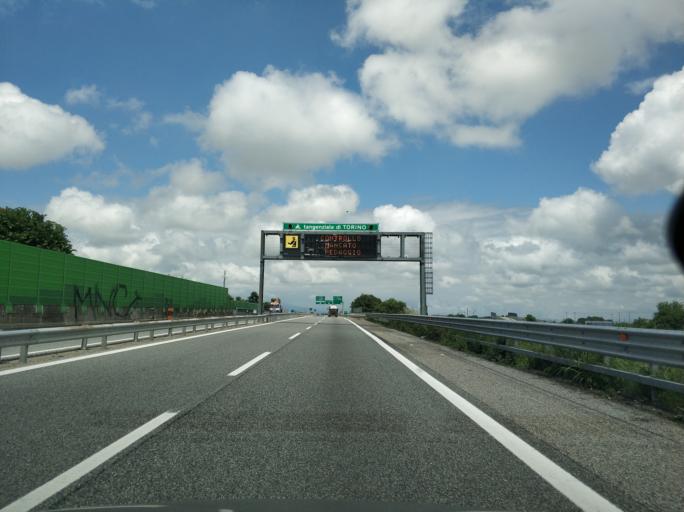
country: IT
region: Piedmont
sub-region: Provincia di Torino
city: Settimo Torinese
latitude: 45.1241
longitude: 7.7324
